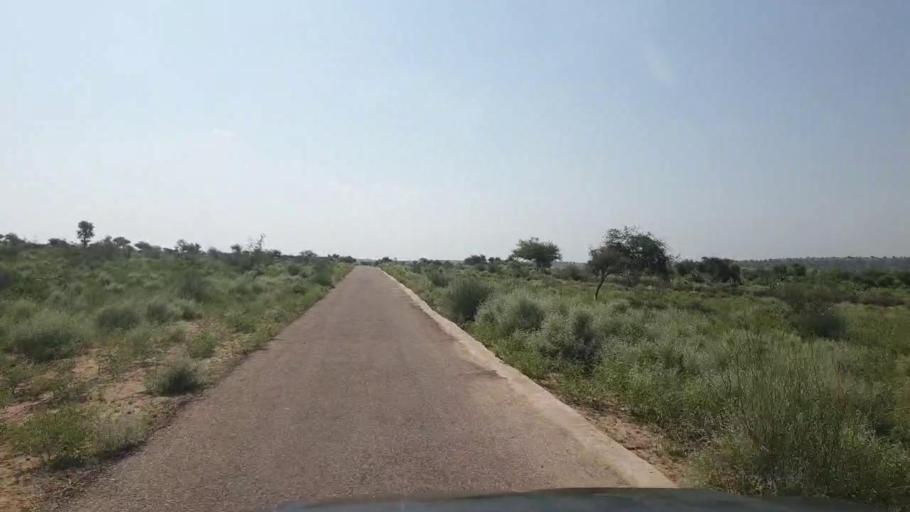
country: PK
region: Sindh
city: Islamkot
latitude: 25.1760
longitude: 70.3964
